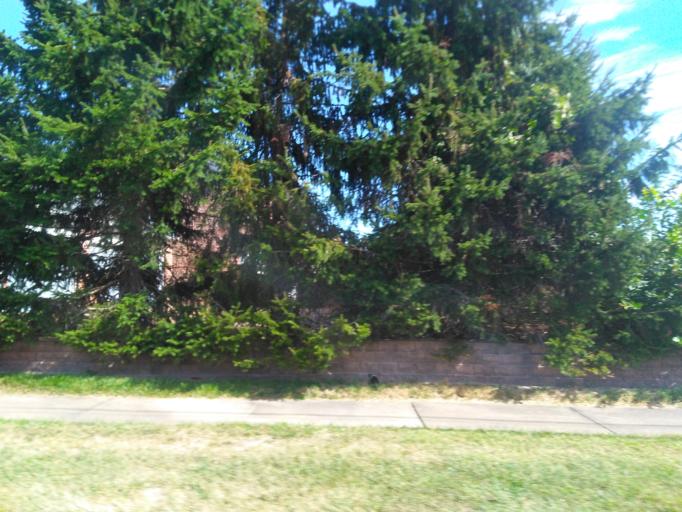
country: US
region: Missouri
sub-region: Saint Louis County
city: Concord
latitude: 38.4892
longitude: -90.3702
